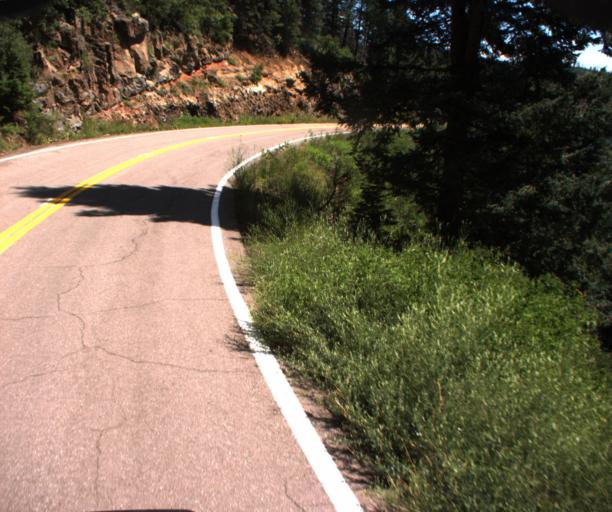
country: US
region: Arizona
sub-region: Greenlee County
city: Morenci
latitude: 33.5682
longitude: -109.3494
